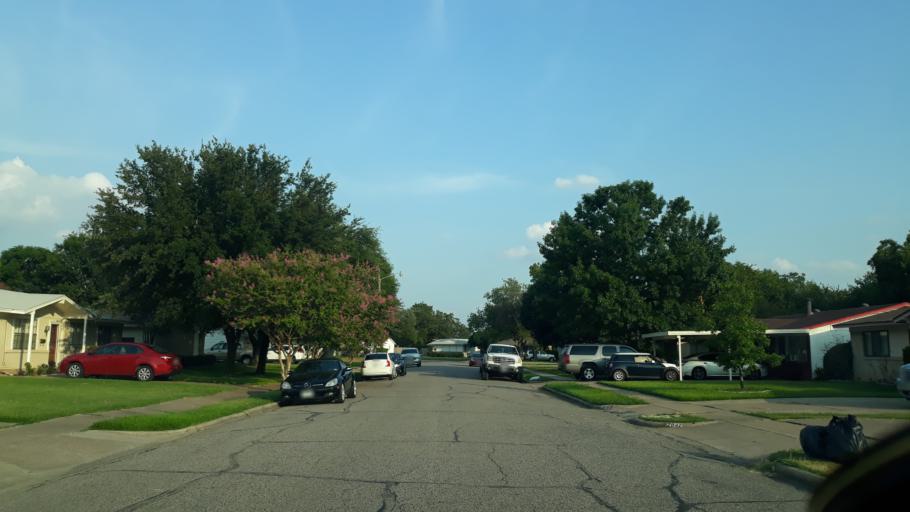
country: US
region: Texas
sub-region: Dallas County
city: Irving
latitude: 32.8455
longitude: -96.9858
